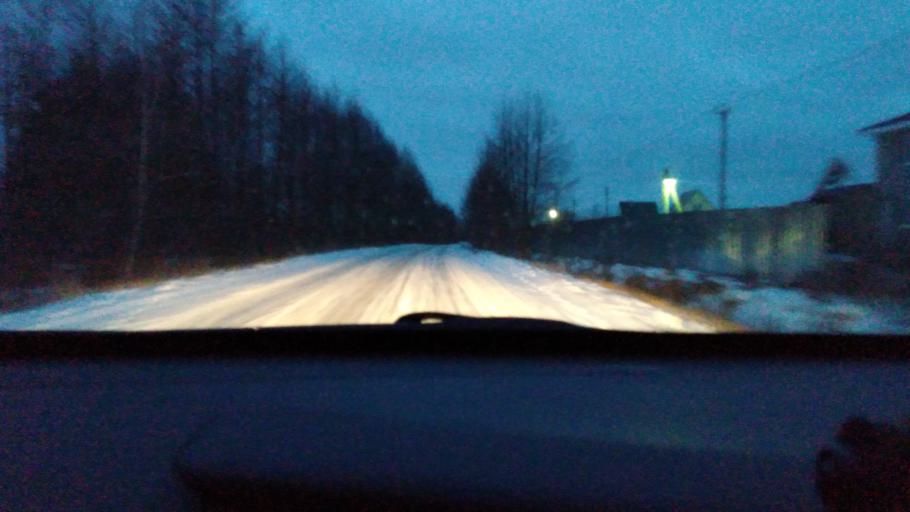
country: RU
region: Moskovskaya
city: Meshcherino
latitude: 55.3157
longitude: 38.3355
